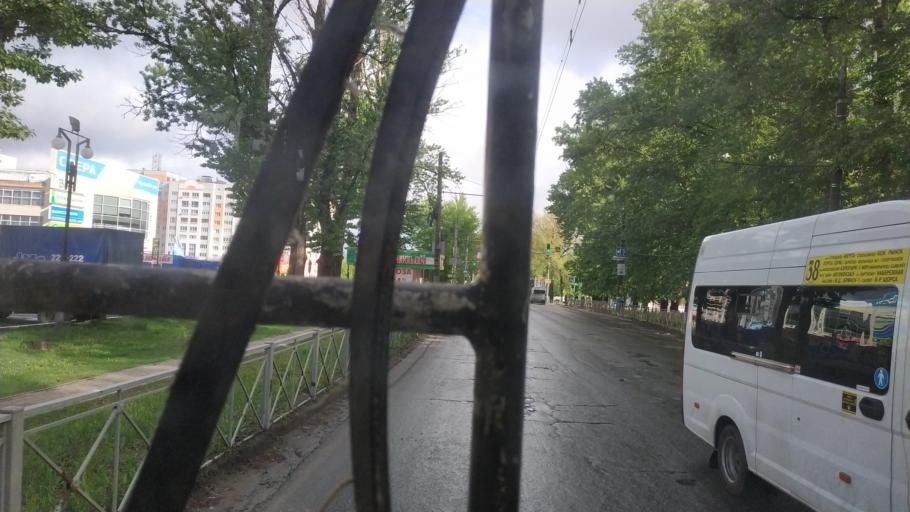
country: RU
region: Brjansk
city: Putevka
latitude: 53.2640
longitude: 34.3236
